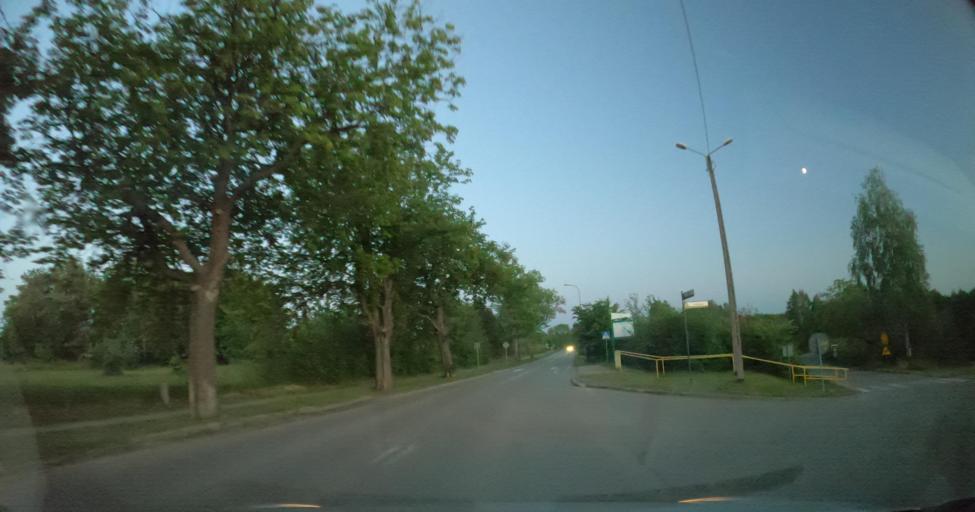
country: PL
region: Pomeranian Voivodeship
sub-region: Powiat wejherowski
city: Szemud
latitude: 54.4770
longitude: 18.2707
